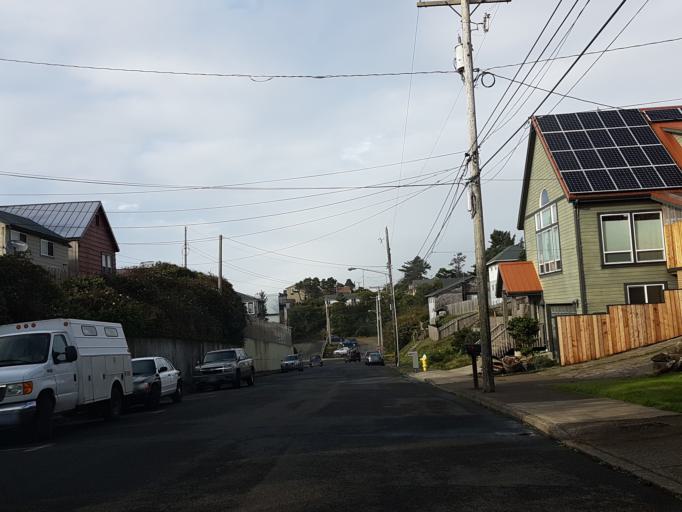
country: US
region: Oregon
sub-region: Lincoln County
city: Newport
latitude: 44.6370
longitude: -124.0590
